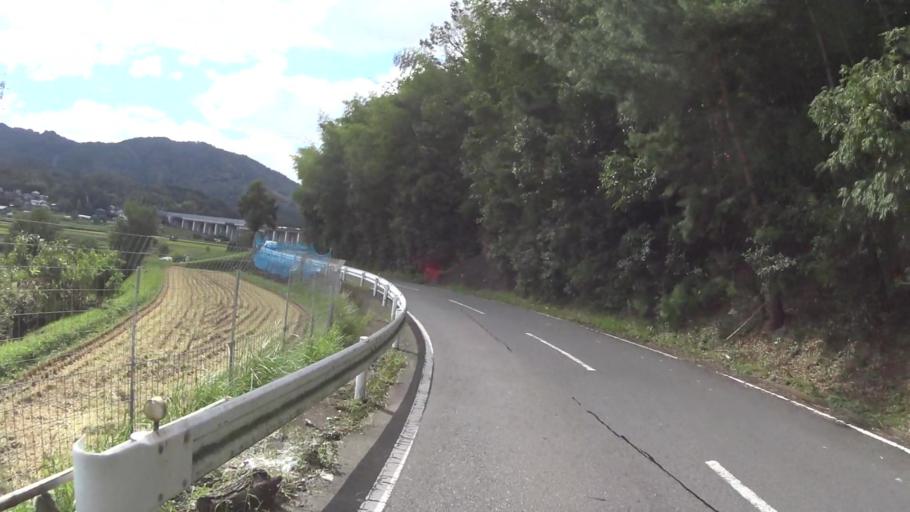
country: JP
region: Shiga Prefecture
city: Otsu-shi
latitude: 34.9474
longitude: 135.8949
